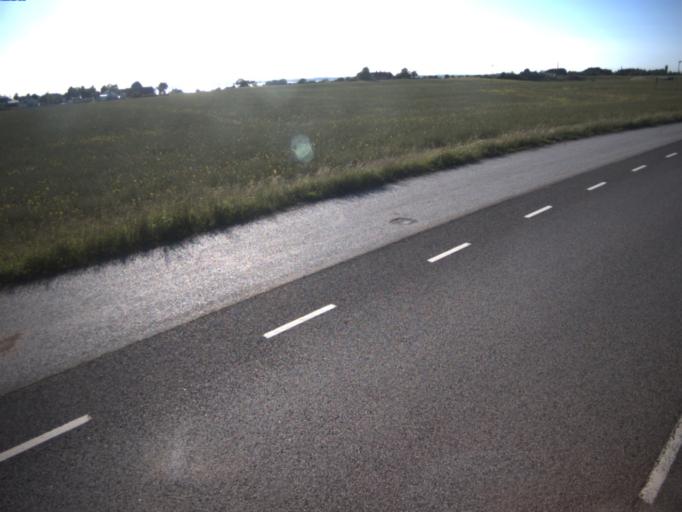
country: SE
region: Skane
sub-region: Helsingborg
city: Rydeback
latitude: 55.9788
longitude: 12.7714
